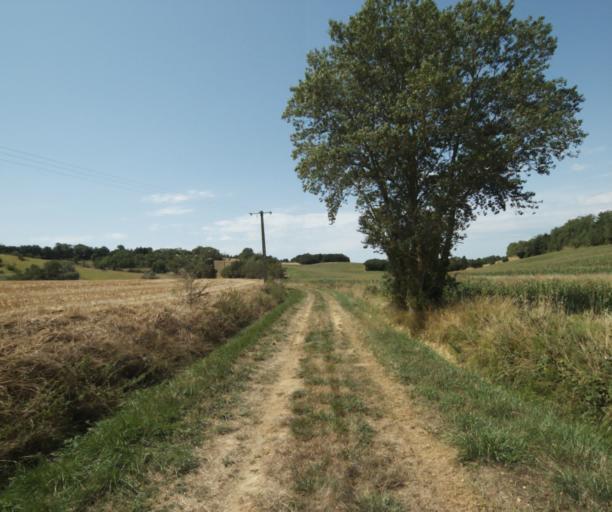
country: FR
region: Midi-Pyrenees
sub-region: Departement de la Haute-Garonne
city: Saint-Felix-Lauragais
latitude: 43.4547
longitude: 1.8632
